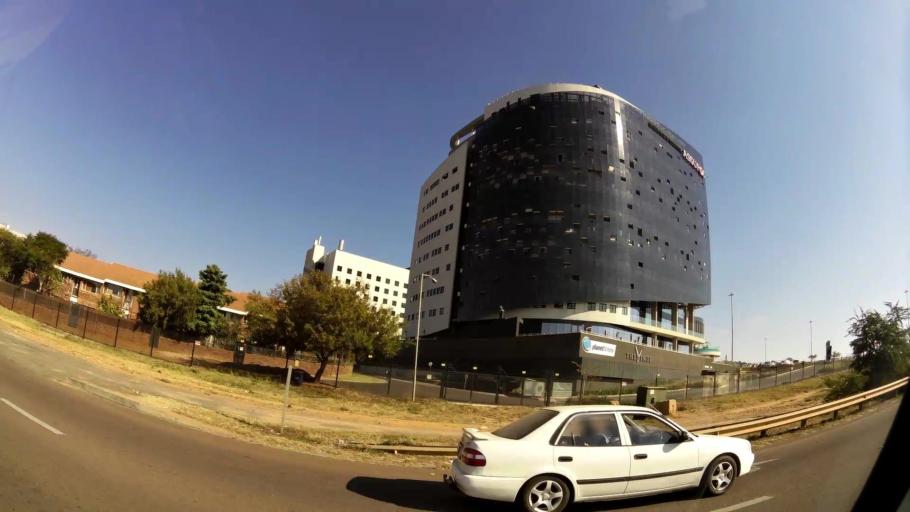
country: ZA
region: Gauteng
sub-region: City of Tshwane Metropolitan Municipality
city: Pretoria
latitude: -25.7850
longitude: 28.2719
